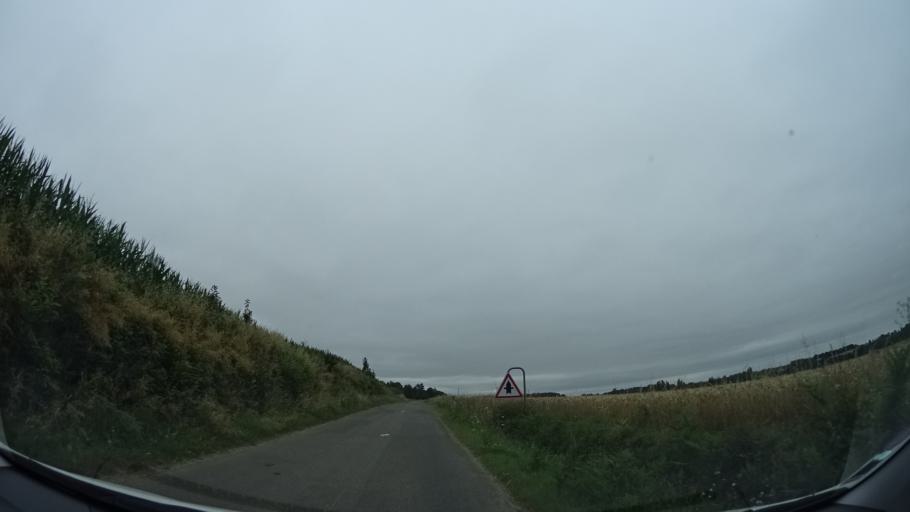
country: FR
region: Brittany
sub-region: Departement des Cotes-d'Armor
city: Evran
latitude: 48.3226
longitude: -1.9327
